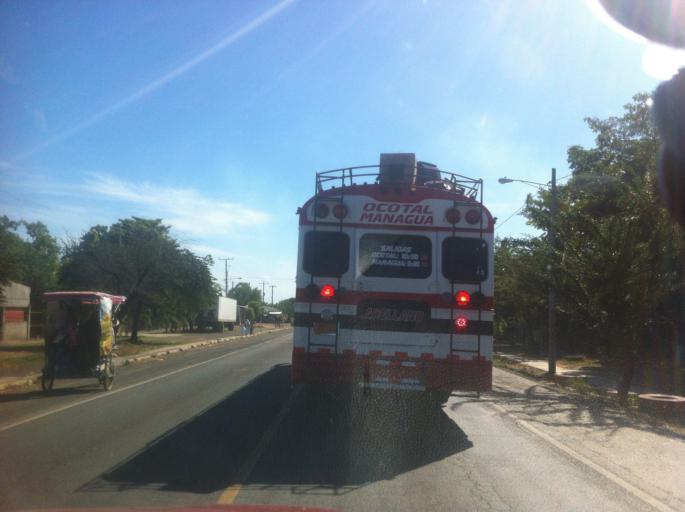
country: NI
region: Managua
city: Tipitapa
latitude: 12.3037
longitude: -86.0556
